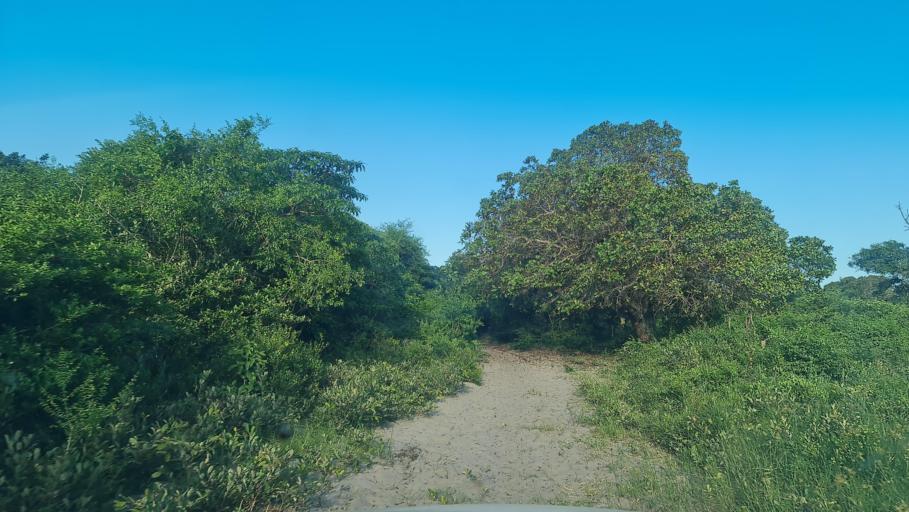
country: MZ
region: Gaza
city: Macia
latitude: -25.2299
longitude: 33.0147
